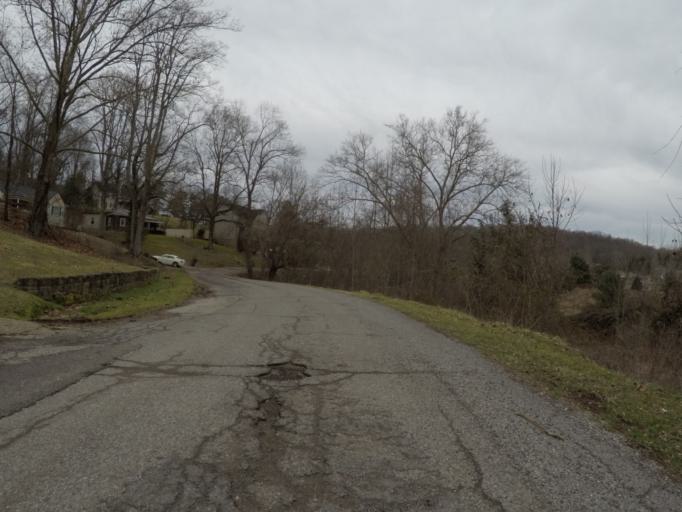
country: US
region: Ohio
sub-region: Lawrence County
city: Burlington
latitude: 38.3819
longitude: -82.5148
